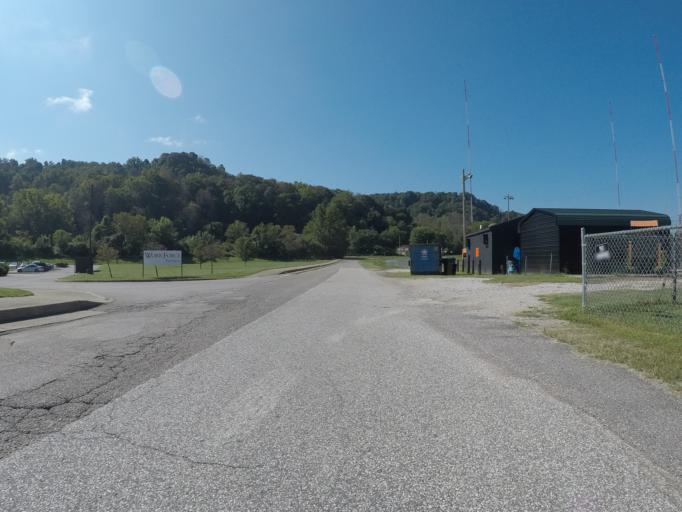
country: US
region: Ohio
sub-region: Lawrence County
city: Burlington
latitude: 38.4019
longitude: -82.4932
